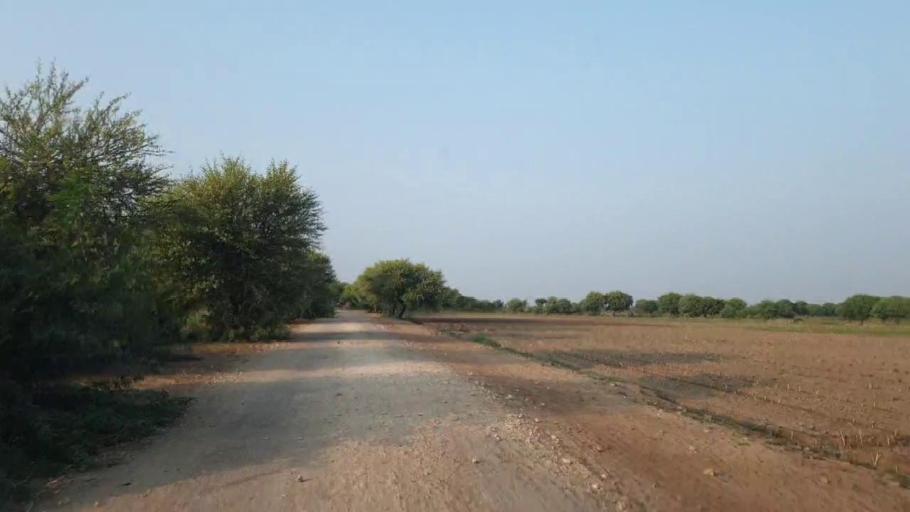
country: PK
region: Sindh
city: Rajo Khanani
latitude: 25.0419
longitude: 68.9644
